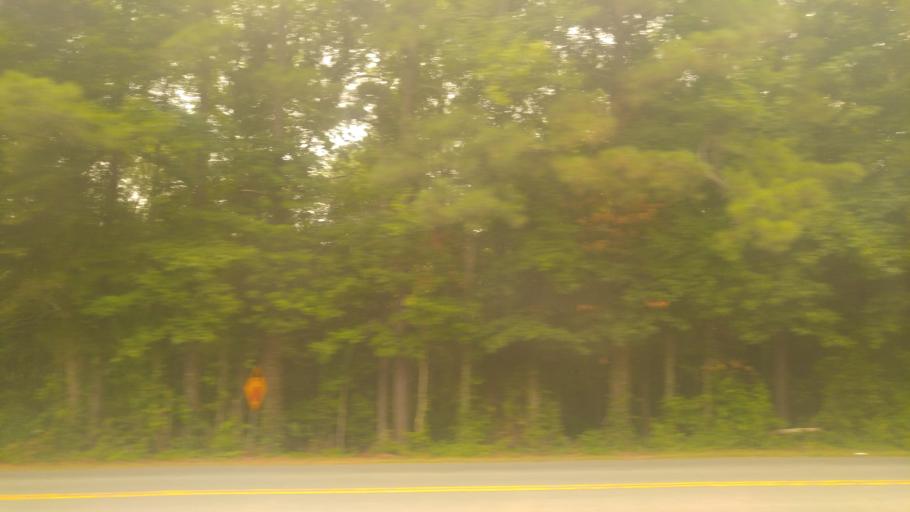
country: US
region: Virginia
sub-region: Hanover County
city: Ashland
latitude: 37.7477
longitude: -77.4848
